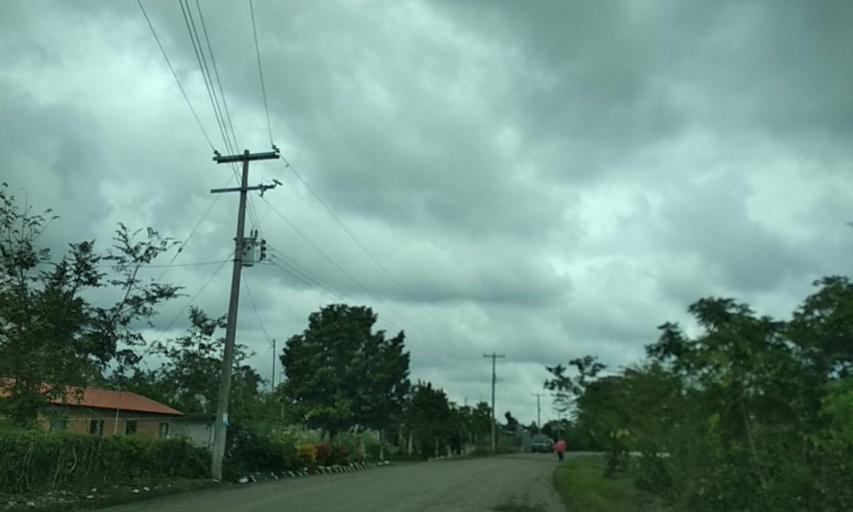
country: MX
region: Puebla
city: Espinal
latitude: 20.3237
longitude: -97.4181
